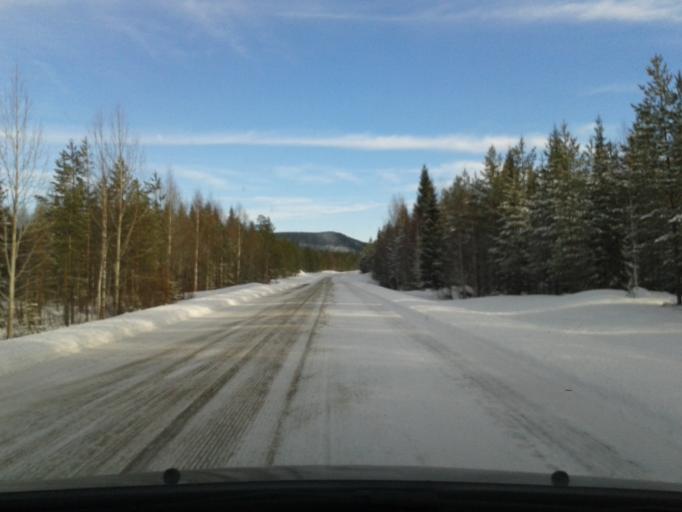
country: SE
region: Vaesterbotten
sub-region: Asele Kommun
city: Asele
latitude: 64.3165
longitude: 17.1514
